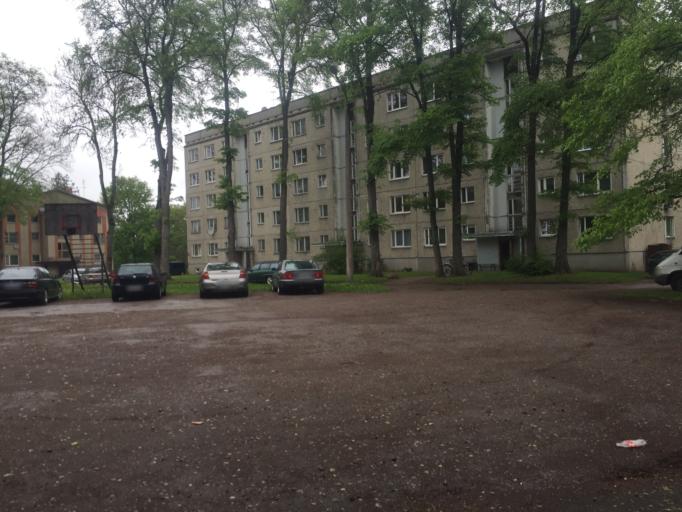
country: LV
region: Lielvarde
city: Lielvarde
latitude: 56.7124
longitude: 24.8364
